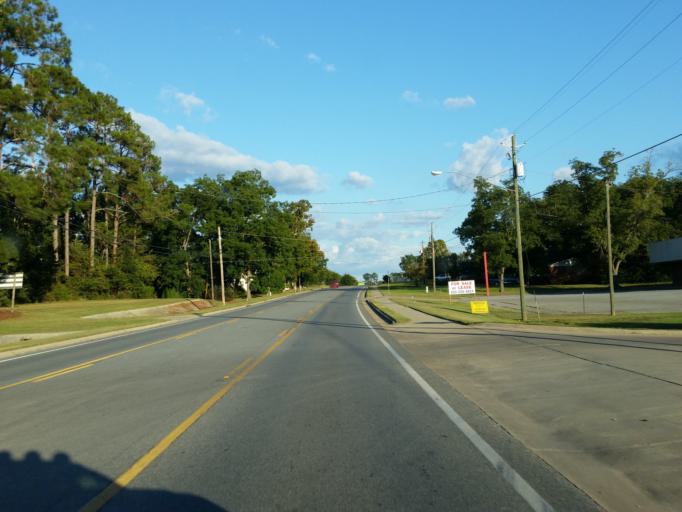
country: US
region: Georgia
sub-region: Dooly County
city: Vienna
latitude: 32.0894
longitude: -83.7795
